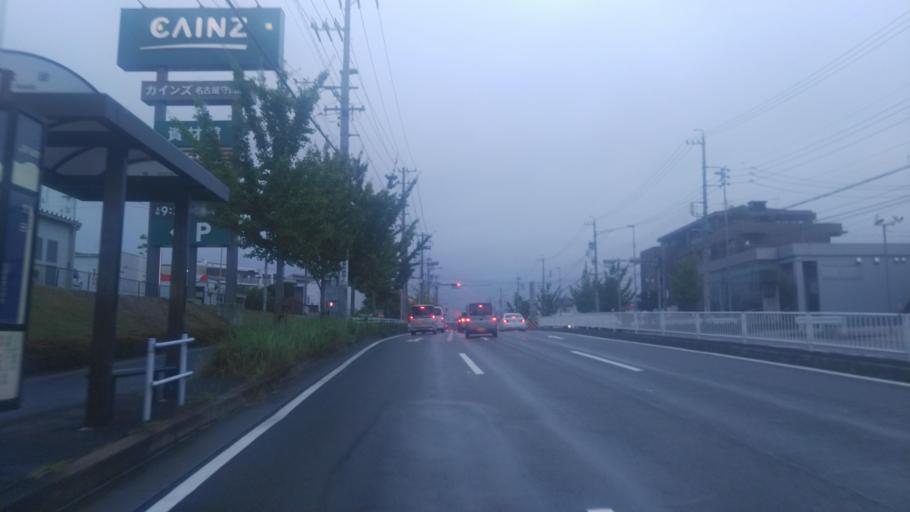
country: JP
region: Aichi
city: Kasugai
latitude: 35.2408
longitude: 137.0140
